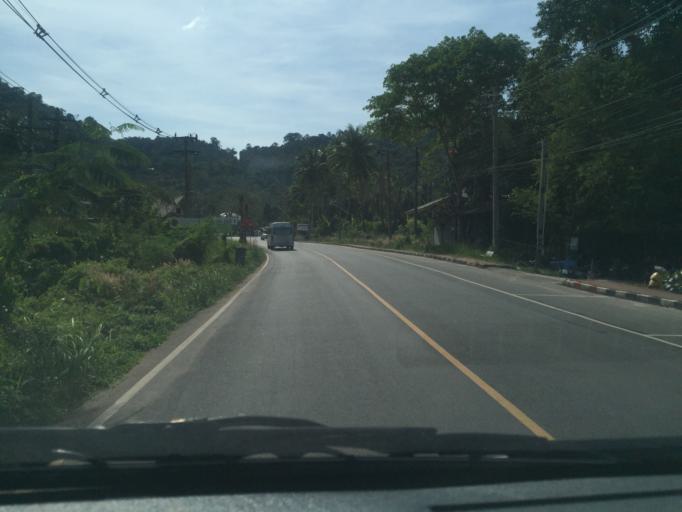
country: TH
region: Trat
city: Laem Ngop
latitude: 12.1295
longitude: 102.2735
